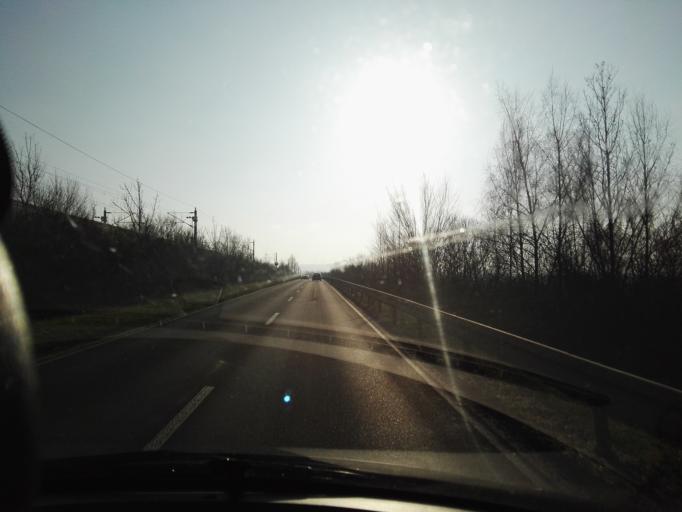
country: DE
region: Lower Saxony
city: Sarstedt
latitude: 52.2019
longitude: 9.8241
